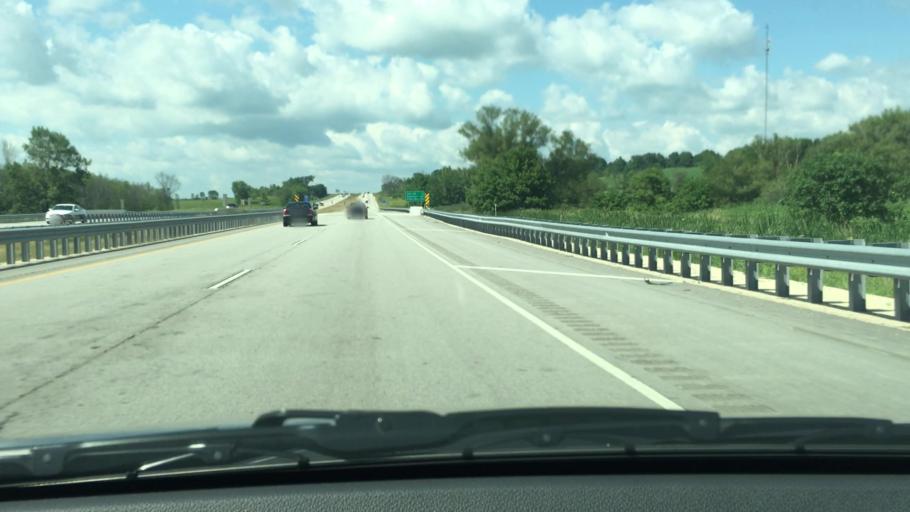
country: US
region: Wisconsin
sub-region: Dodge County
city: Theresa
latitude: 43.4826
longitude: -88.3667
